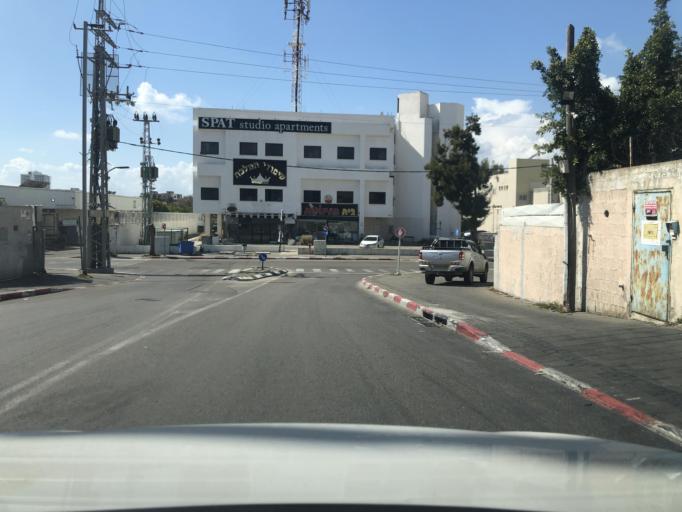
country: IL
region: Tel Aviv
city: Bat Yam
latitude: 32.0116
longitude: 34.7509
